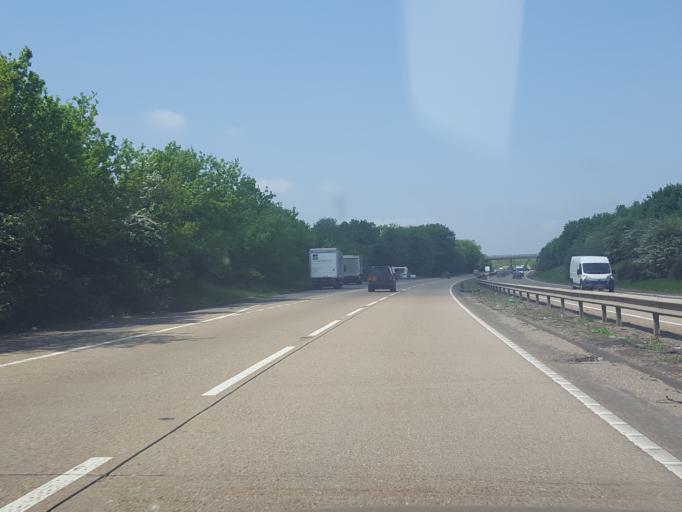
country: GB
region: England
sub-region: Essex
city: Alresford
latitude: 51.8887
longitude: 1.0164
